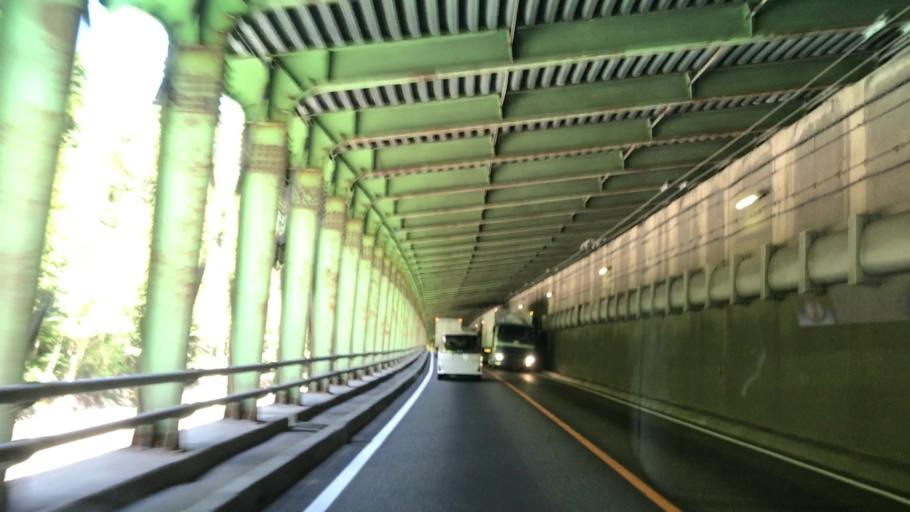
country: JP
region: Hokkaido
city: Shimo-furano
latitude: 42.9393
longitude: 142.6023
